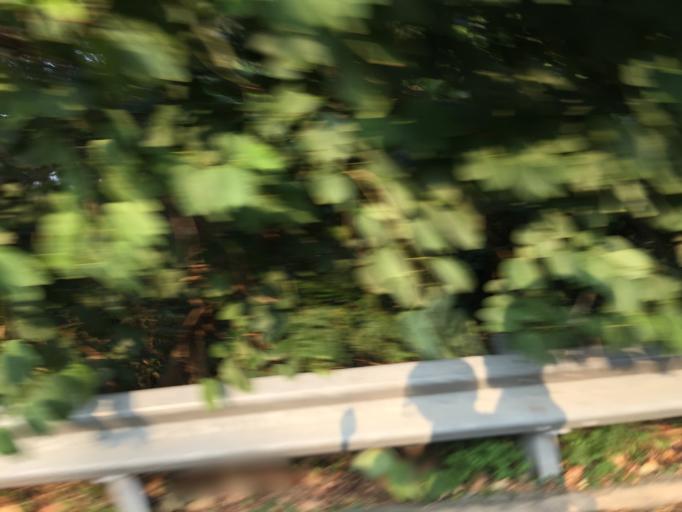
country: TW
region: Taiwan
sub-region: Hsinchu
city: Hsinchu
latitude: 24.7884
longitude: 120.9477
